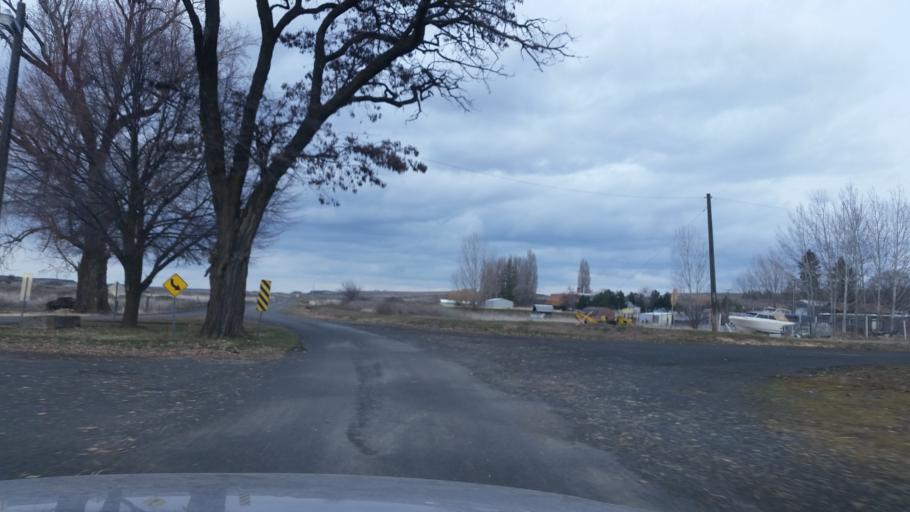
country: US
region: Washington
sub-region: Spokane County
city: Medical Lake
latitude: 47.2016
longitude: -117.9059
